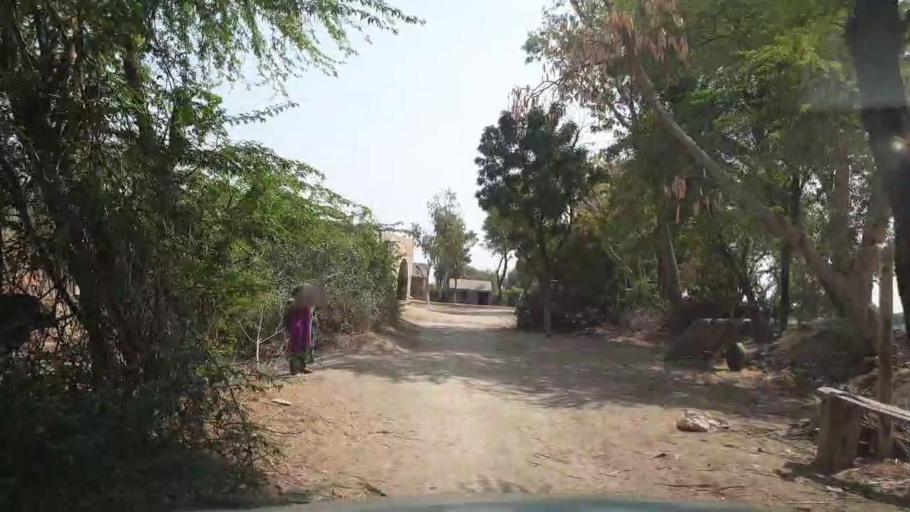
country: PK
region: Sindh
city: Dhoro Naro
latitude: 25.4562
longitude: 69.6317
